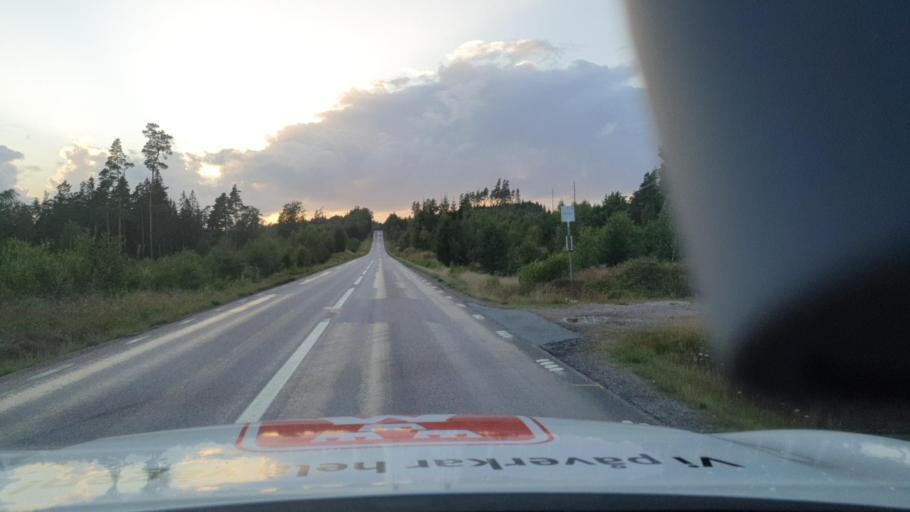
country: SE
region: Vaestra Goetaland
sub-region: Svenljunga Kommun
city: Svenljunga
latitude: 57.4833
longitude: 13.0107
